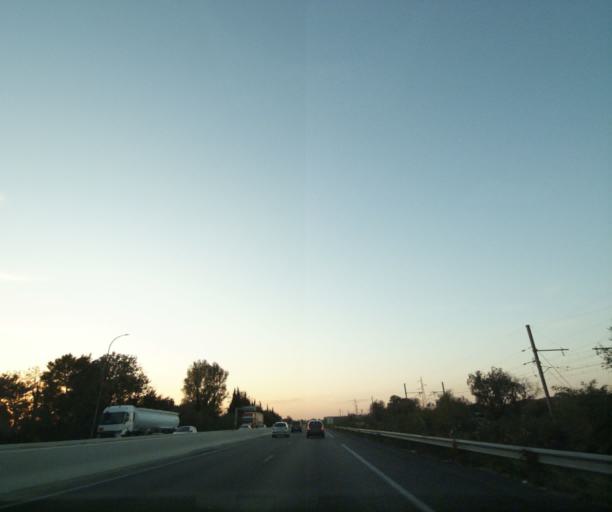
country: FR
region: Provence-Alpes-Cote d'Azur
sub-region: Departement des Bouches-du-Rhone
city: Arles
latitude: 43.6526
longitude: 4.6672
